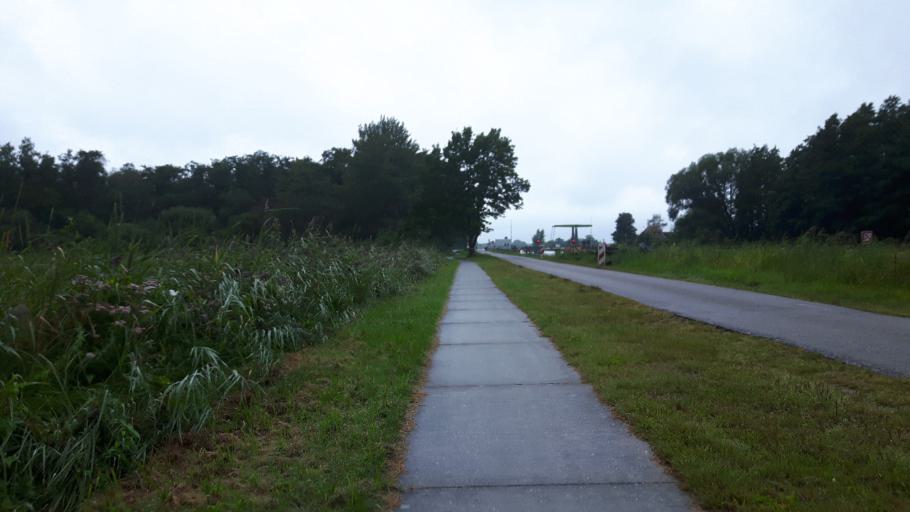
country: NL
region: Overijssel
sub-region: Gemeente Steenwijkerland
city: Oldemarkt
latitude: 52.7973
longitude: 5.9879
